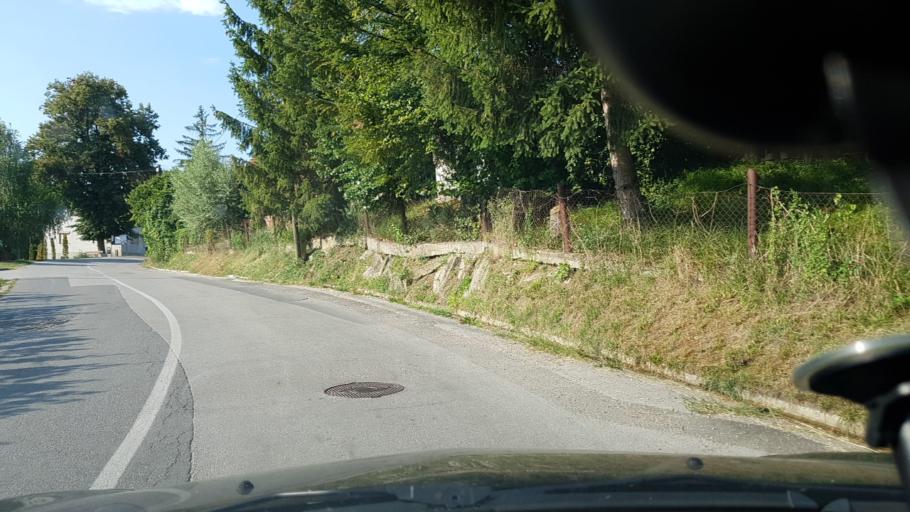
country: HR
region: Zagrebacka
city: Bregana
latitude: 45.8929
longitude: 15.6861
